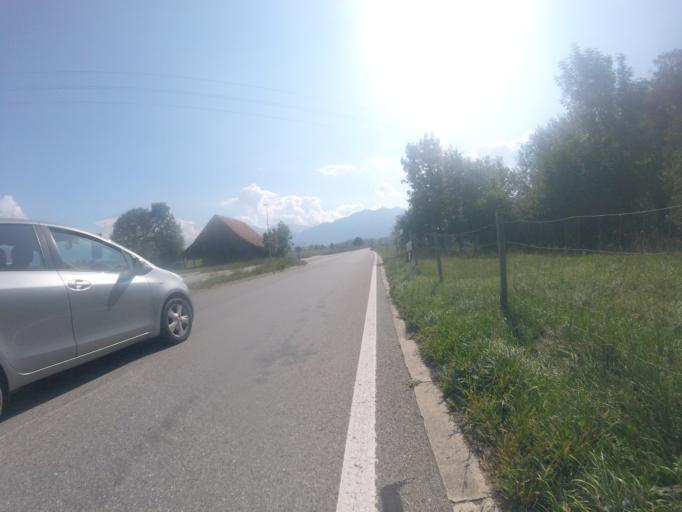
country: CH
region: Bern
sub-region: Thun District
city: Uttigen
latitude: 46.7859
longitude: 7.5741
